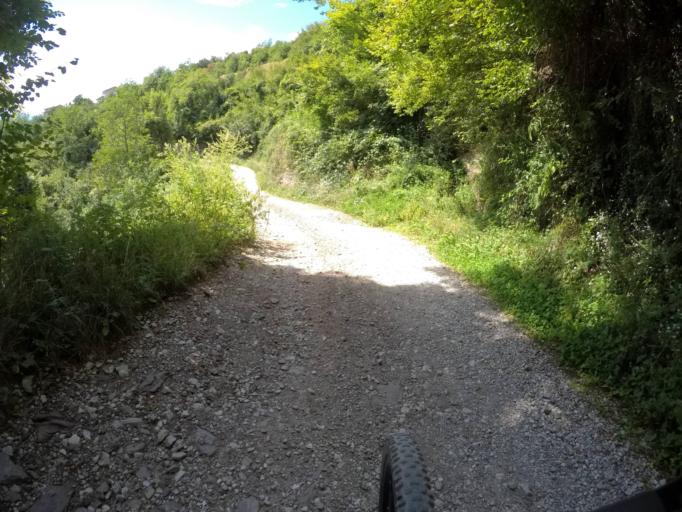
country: IT
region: Friuli Venezia Giulia
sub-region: Provincia di Udine
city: Zuglio
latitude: 46.4682
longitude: 13.0408
